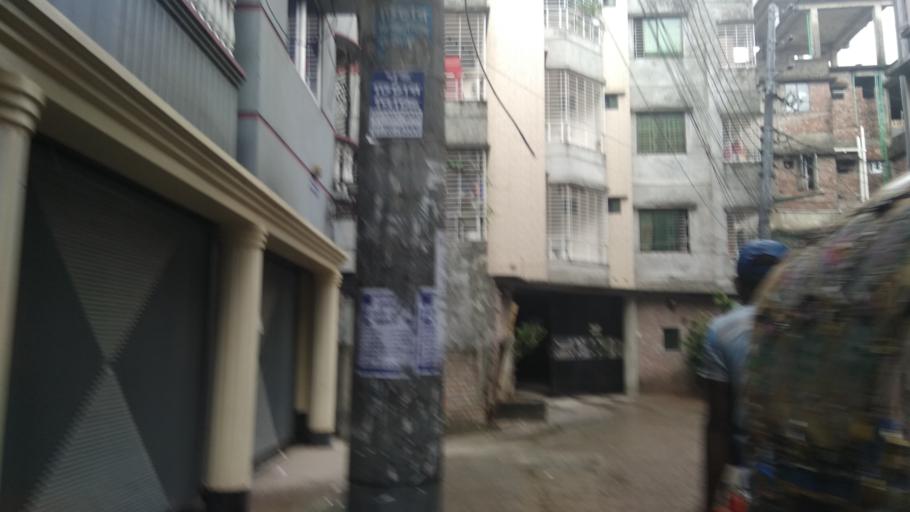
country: BD
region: Dhaka
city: Azimpur
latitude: 23.7976
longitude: 90.3829
